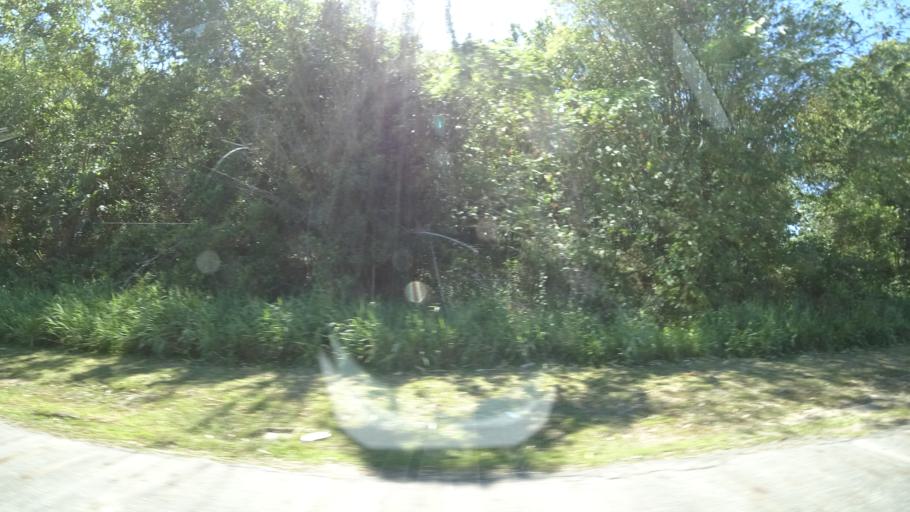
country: BN
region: Brunei and Muara
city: Bandar Seri Begawan
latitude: 4.8981
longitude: 114.9110
